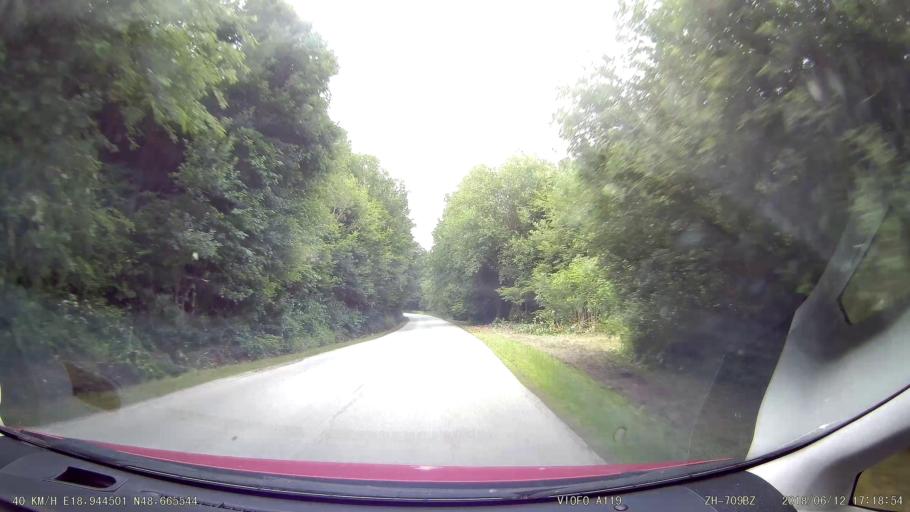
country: SK
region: Banskobystricky
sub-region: Okres Ziar nad Hronom
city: Kremnica
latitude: 48.6656
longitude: 18.9445
